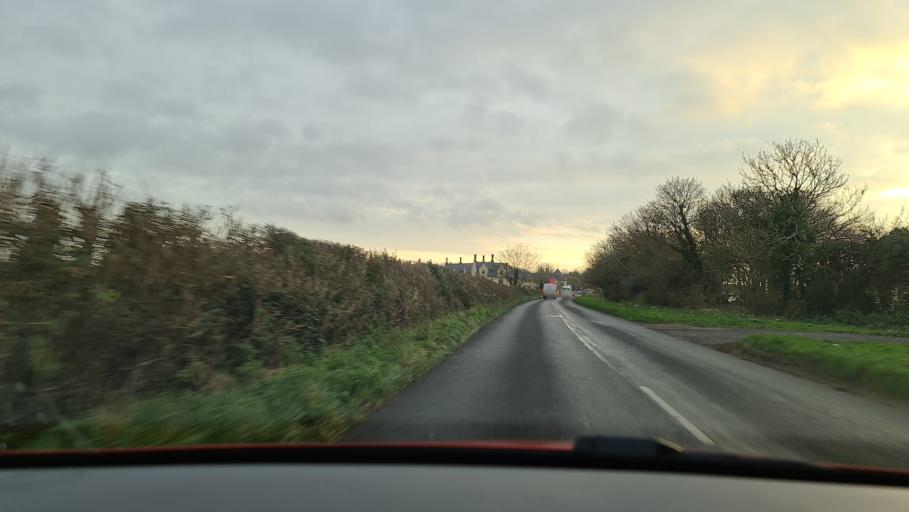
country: GB
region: England
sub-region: Oxfordshire
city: Kidlington
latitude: 51.8567
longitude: -1.2807
